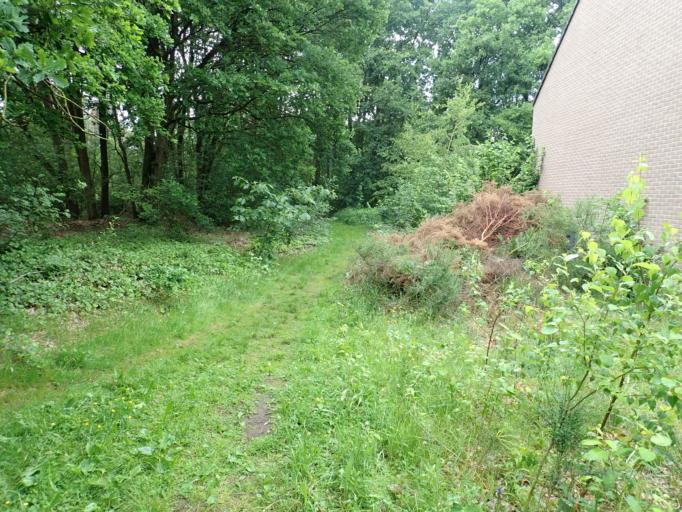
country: BE
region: Flanders
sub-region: Provincie Antwerpen
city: Oud-Turnhout
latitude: 51.3272
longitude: 5.0036
